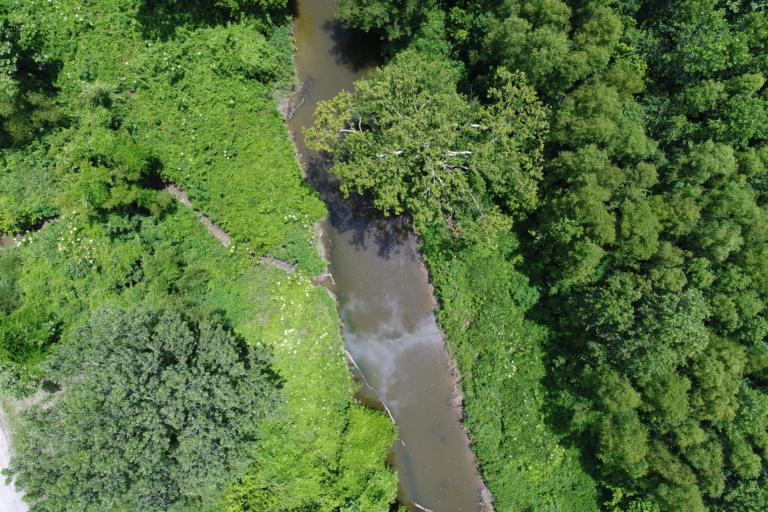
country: US
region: Mississippi
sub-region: De Soto County
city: Walls
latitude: 34.9188
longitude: -90.1708
